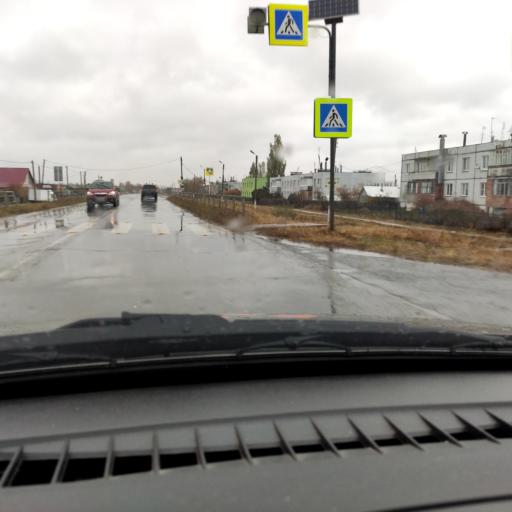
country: RU
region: Samara
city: Tol'yatti
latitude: 53.6409
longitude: 49.2968
